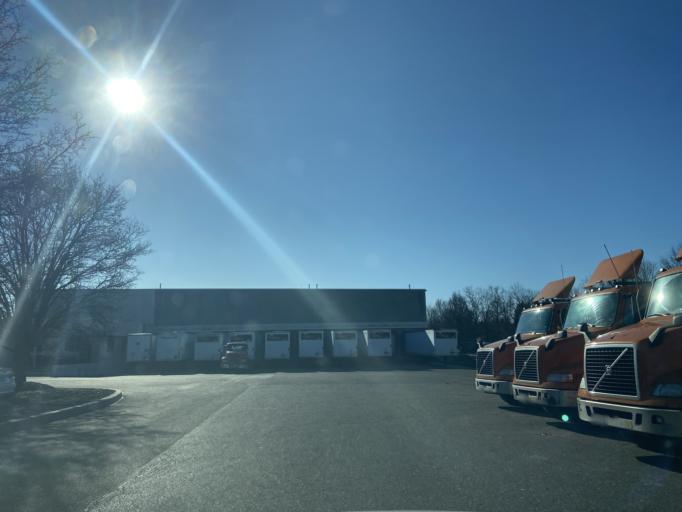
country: US
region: New Jersey
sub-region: Cumberland County
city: Vineland
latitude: 39.4949
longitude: -75.0692
